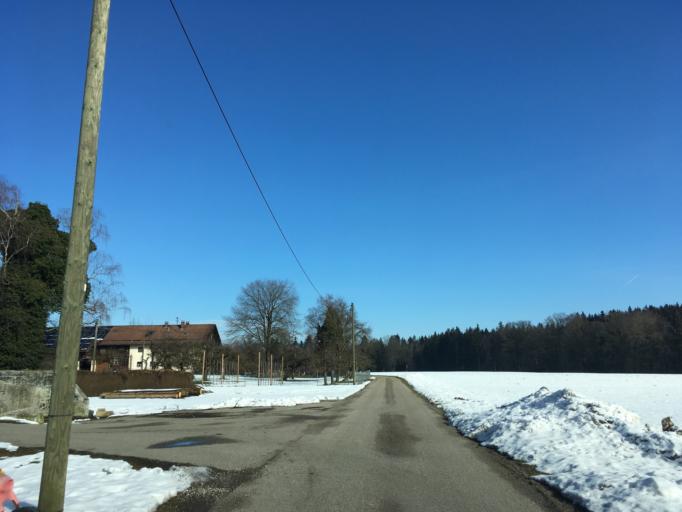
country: DE
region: Bavaria
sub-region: Upper Bavaria
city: Schechen
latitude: 47.9128
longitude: 12.1504
